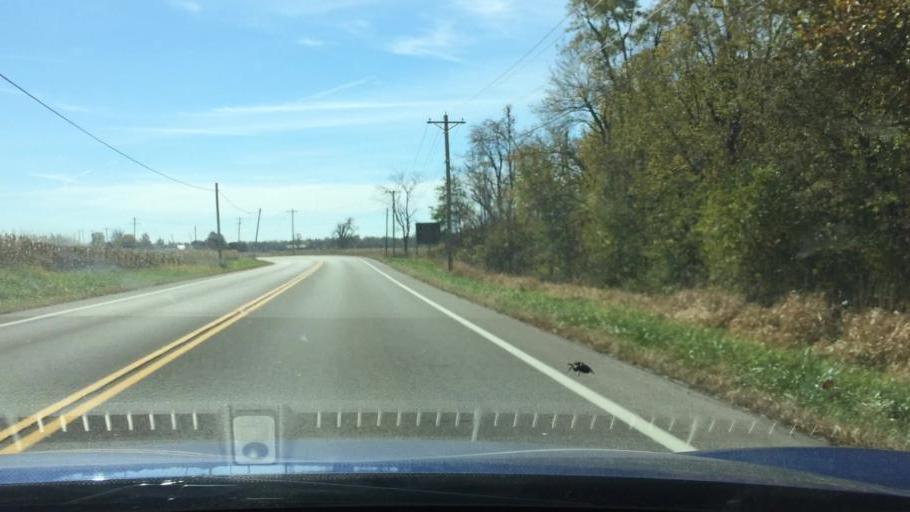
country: US
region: Ohio
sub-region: Logan County
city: Russells Point
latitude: 40.4444
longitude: -83.9053
